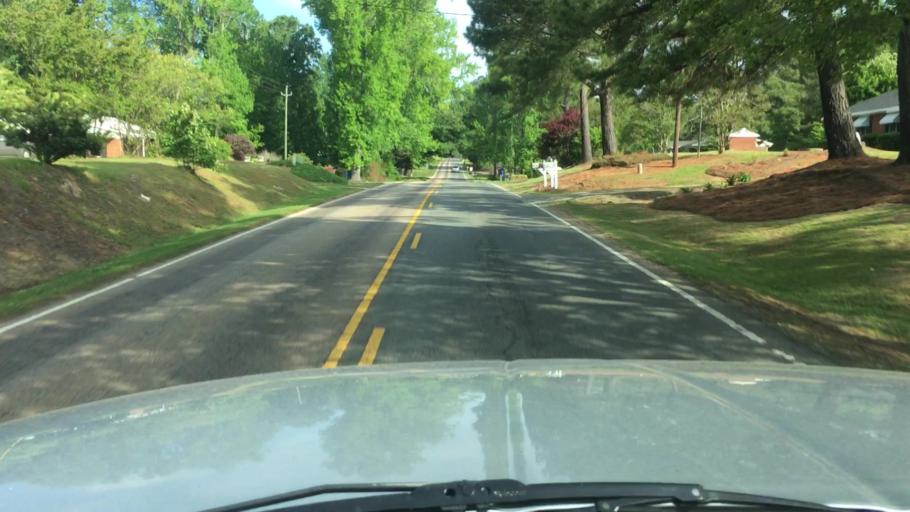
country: US
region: North Carolina
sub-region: Johnston County
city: Wilsons Mills
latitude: 35.6366
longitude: -78.3346
